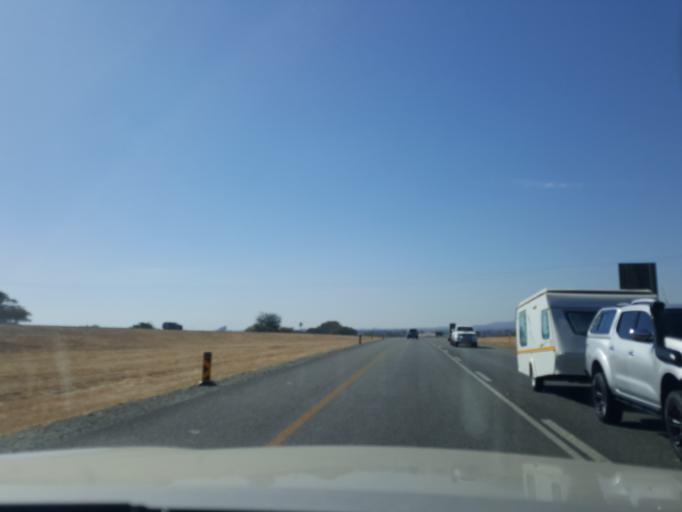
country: ZA
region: North-West
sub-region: Bojanala Platinum District Municipality
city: Brits
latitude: -25.6835
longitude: 27.7848
